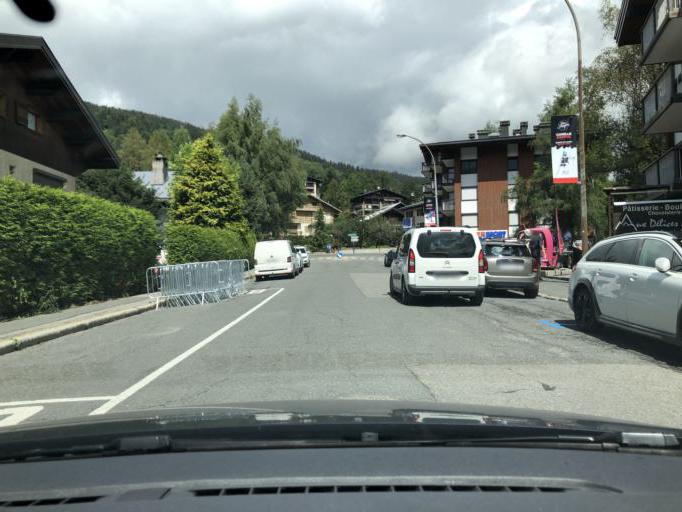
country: FR
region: Rhone-Alpes
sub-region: Departement de la Haute-Savoie
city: Megeve
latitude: 45.8615
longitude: 6.6186
